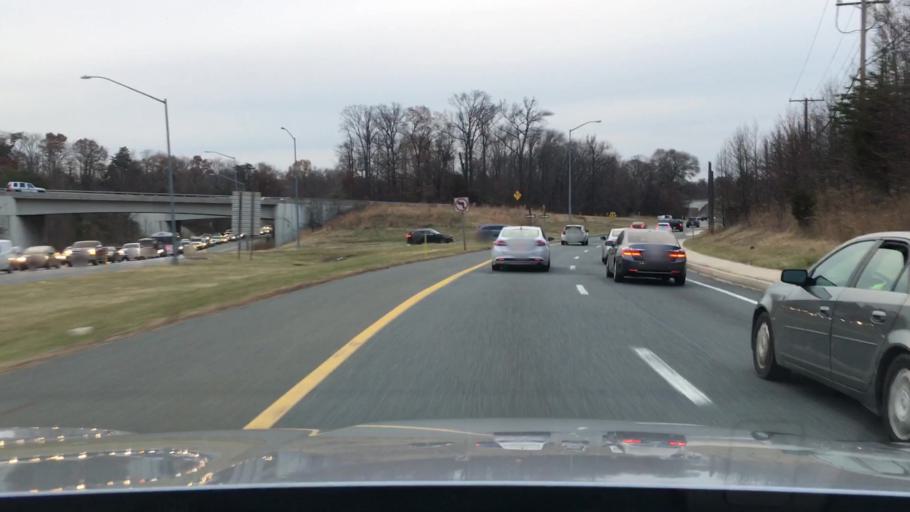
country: US
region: Maryland
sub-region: Prince George's County
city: South Laurel
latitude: 39.0541
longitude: -76.8379
